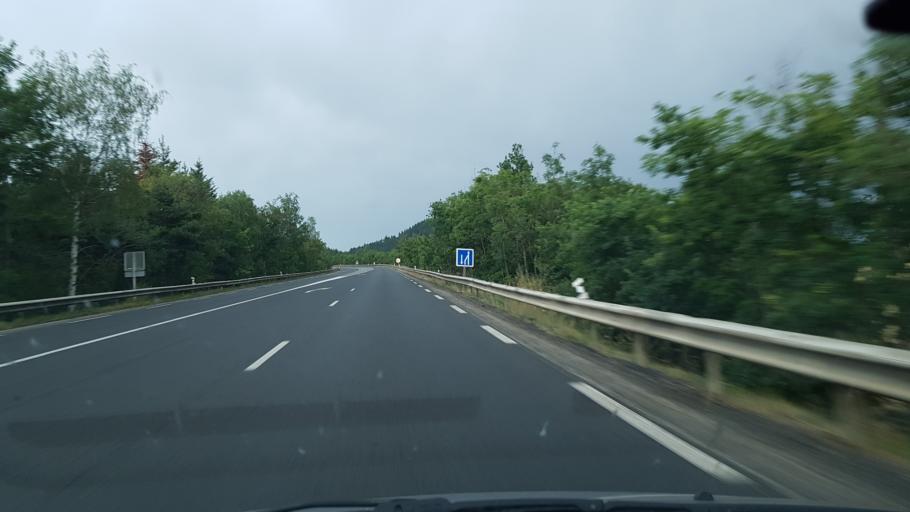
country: FR
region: Auvergne
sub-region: Departement de la Haute-Loire
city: Paulhaguet
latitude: 45.1371
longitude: 3.6006
